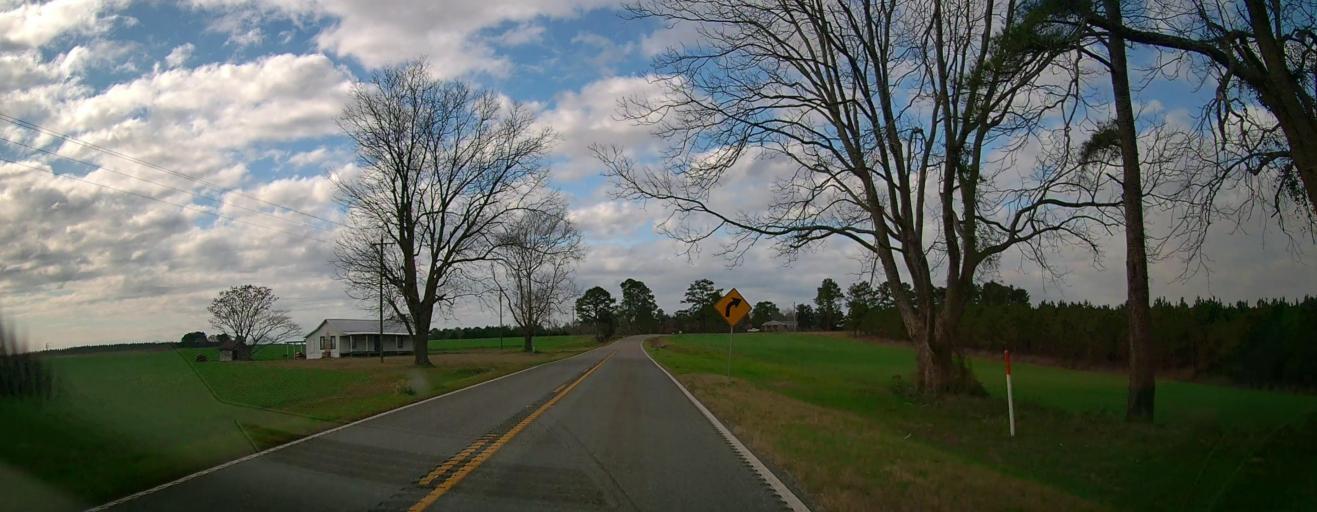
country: US
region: Georgia
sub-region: Marion County
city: Buena Vista
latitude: 32.4413
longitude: -84.4379
